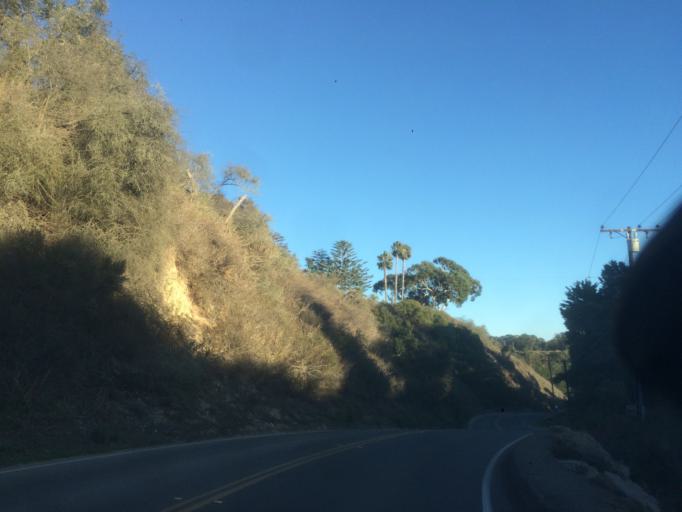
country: US
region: California
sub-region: Santa Barbara County
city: Santa Barbara
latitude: 34.4057
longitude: -119.7477
